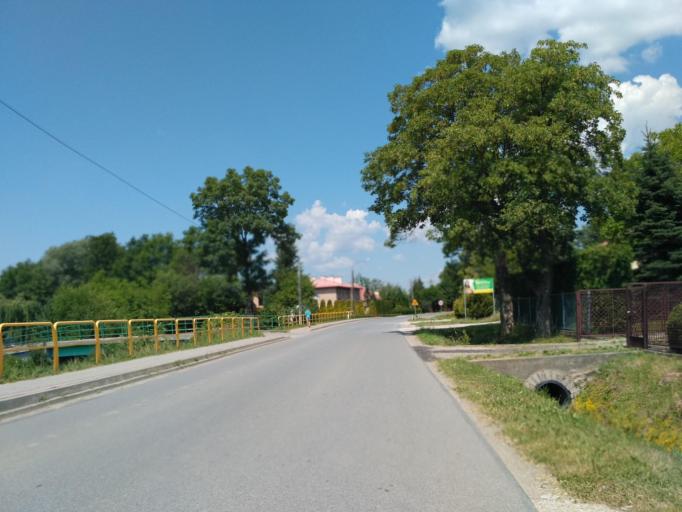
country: PL
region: Subcarpathian Voivodeship
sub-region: Powiat sanocki
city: Niebieszczany
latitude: 49.5260
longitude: 22.1280
